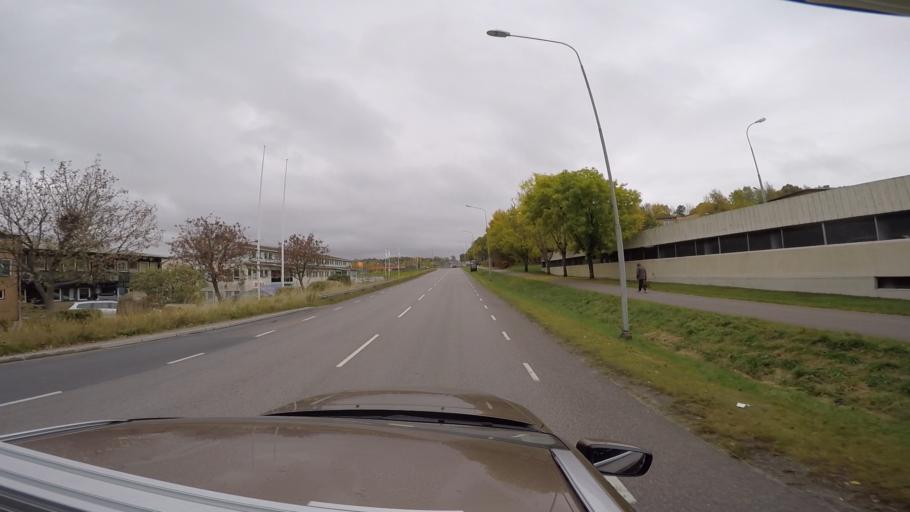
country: SE
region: Vaestra Goetaland
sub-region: Goteborg
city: Majorna
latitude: 57.6431
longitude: 11.9400
